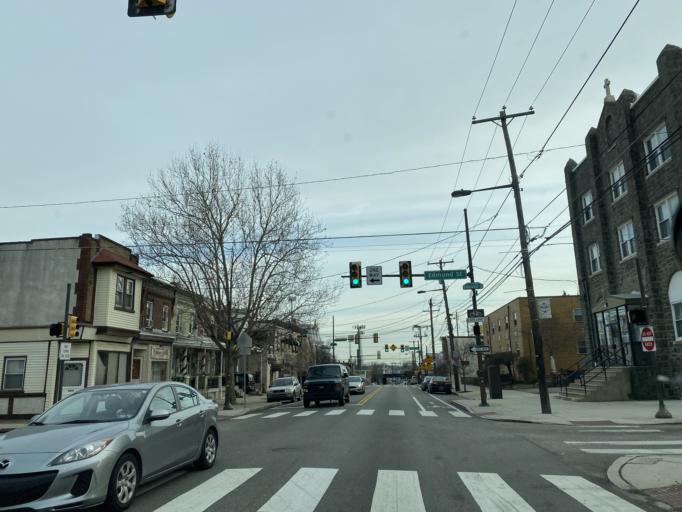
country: US
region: New Jersey
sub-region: Burlington County
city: Palmyra
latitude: 40.0268
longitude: -75.0378
